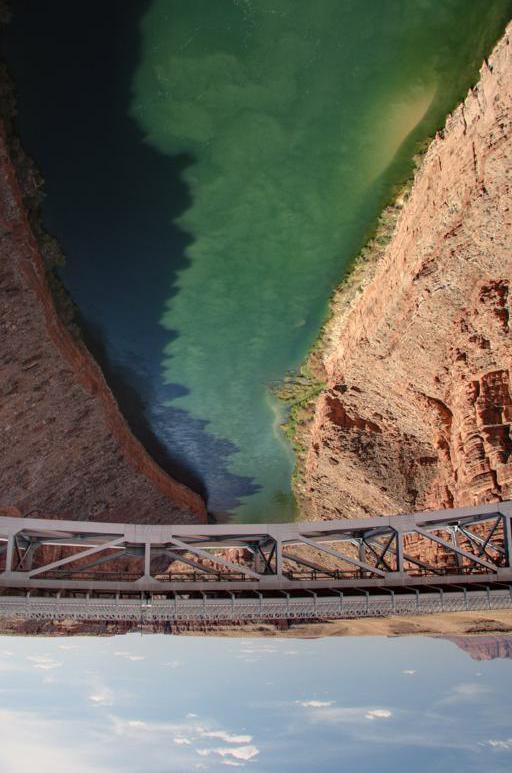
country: US
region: Arizona
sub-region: Coconino County
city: Page
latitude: 36.8177
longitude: -111.6314
